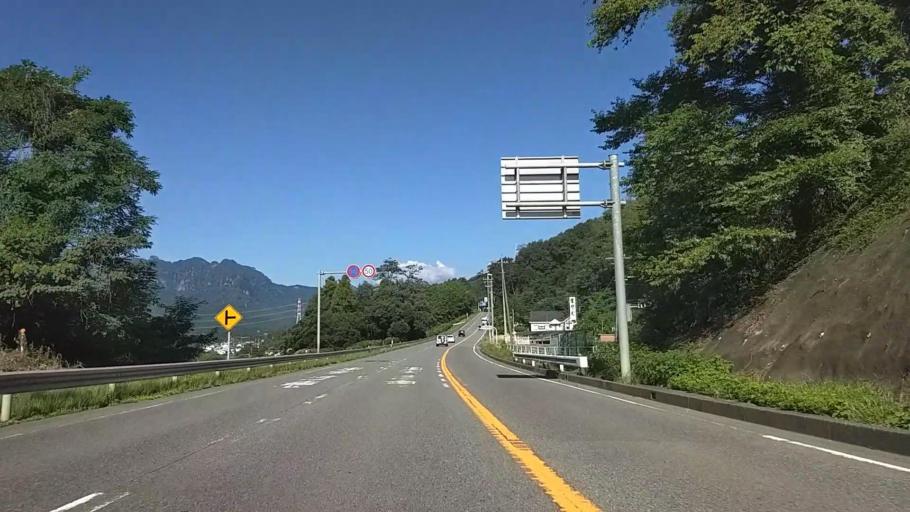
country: JP
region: Gunma
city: Annaka
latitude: 36.3177
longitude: 138.7975
